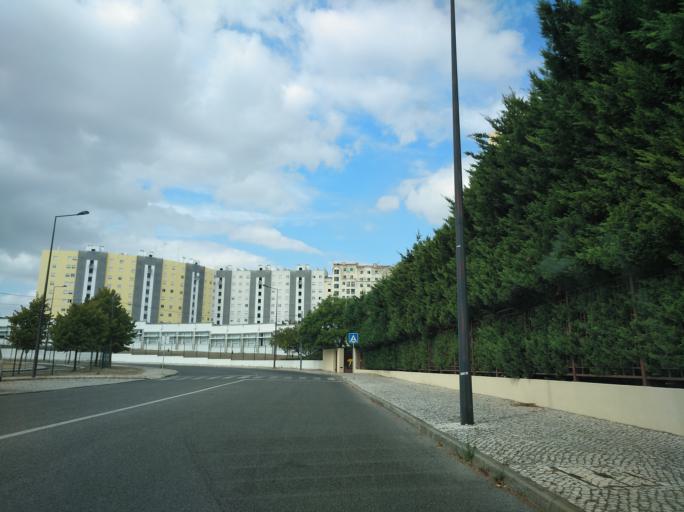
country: PT
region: Lisbon
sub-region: Lisbon
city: Lisbon
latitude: 38.7432
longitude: -9.1203
